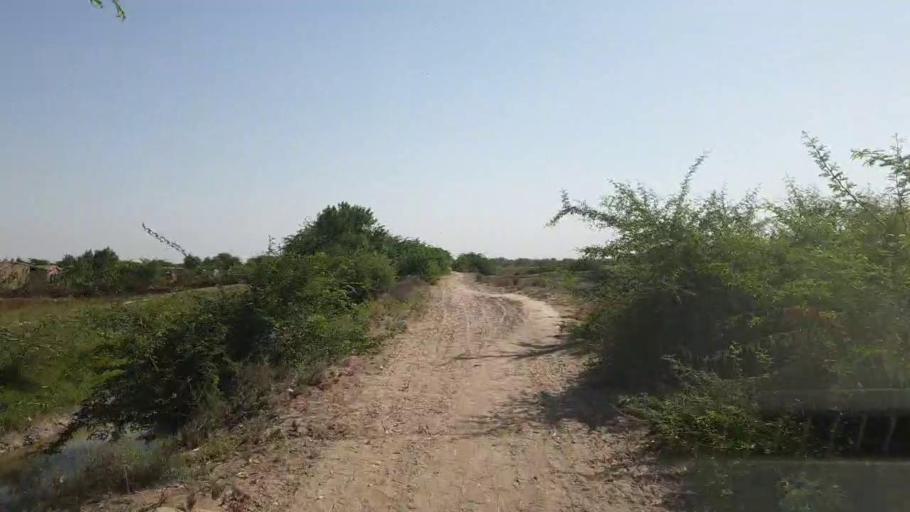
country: PK
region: Sindh
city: Kadhan
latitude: 24.5904
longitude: 69.0083
